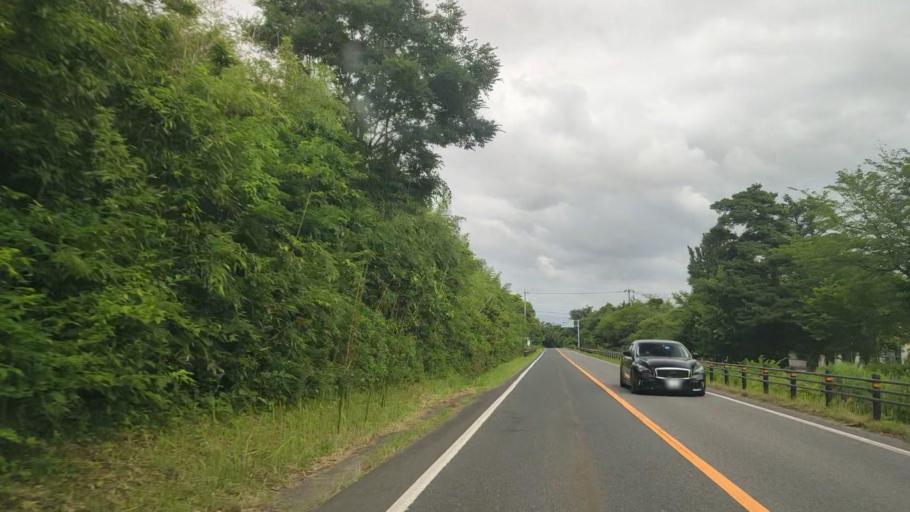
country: JP
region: Tottori
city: Yonago
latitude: 35.4218
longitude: 133.4298
